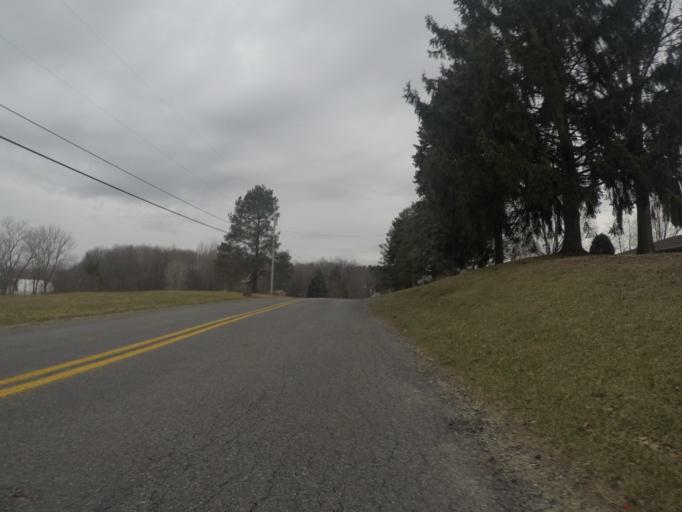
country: US
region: Ohio
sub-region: Portage County
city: Ravenna
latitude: 41.1800
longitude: -81.2956
